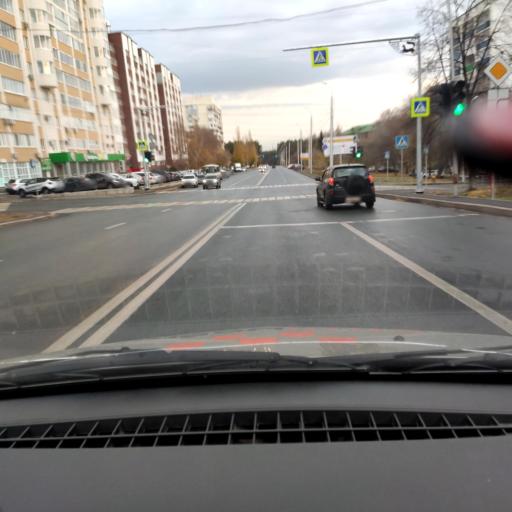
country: RU
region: Bashkortostan
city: Ufa
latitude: 54.7908
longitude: 56.0416
